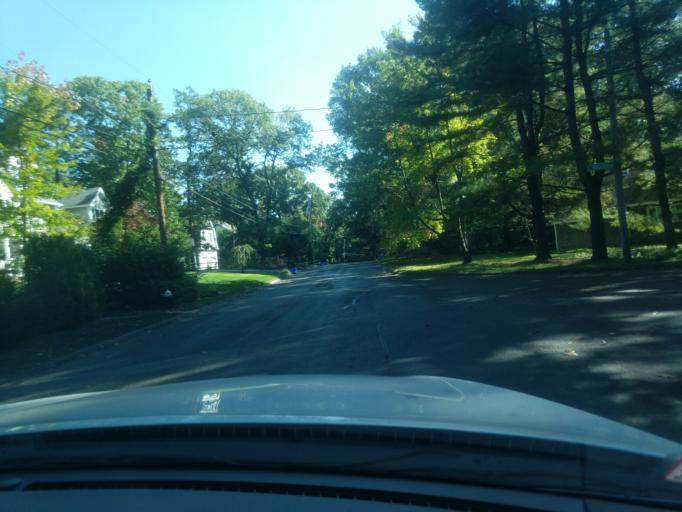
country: US
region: Massachusetts
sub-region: Middlesex County
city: Lexington
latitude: 42.4308
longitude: -71.2411
